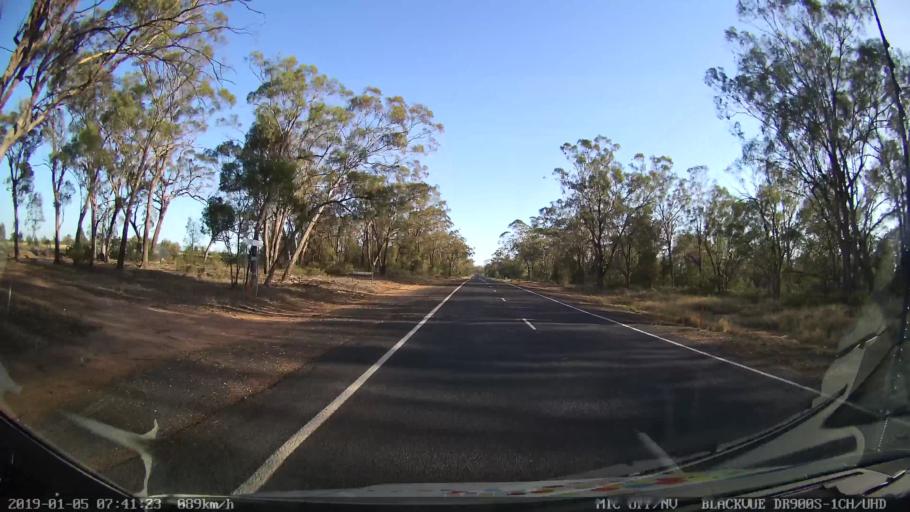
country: AU
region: New South Wales
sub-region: Gilgandra
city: Gilgandra
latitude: -31.9115
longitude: 148.6208
